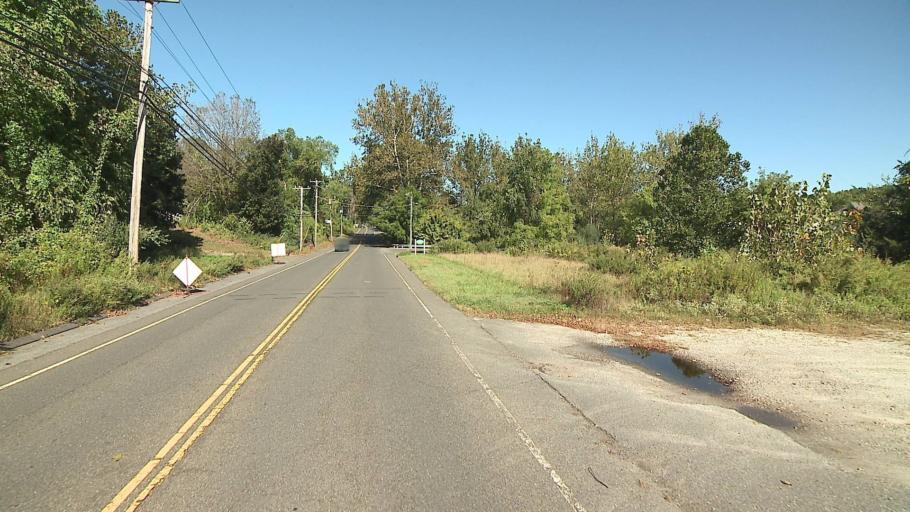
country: US
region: Connecticut
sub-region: Litchfield County
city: New Milford
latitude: 41.4854
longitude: -73.4113
